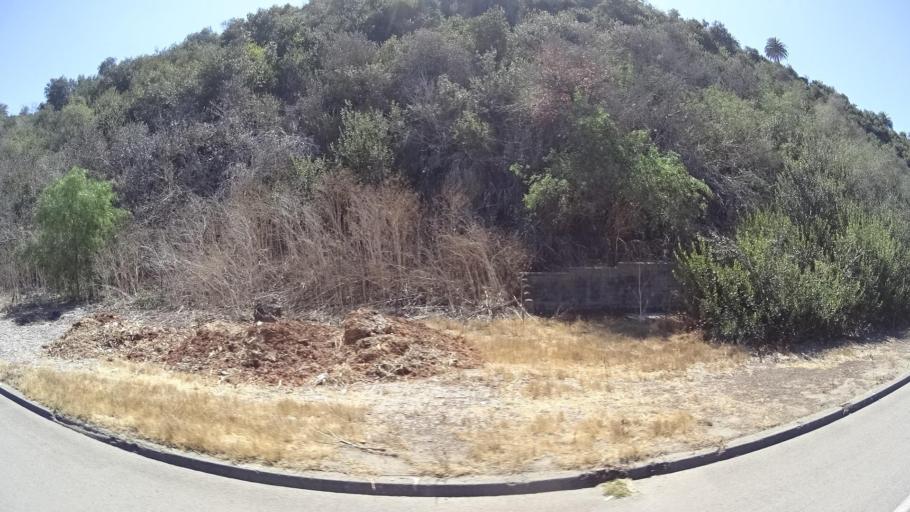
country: US
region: California
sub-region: San Diego County
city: Fairbanks Ranch
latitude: 32.9744
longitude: -117.2172
